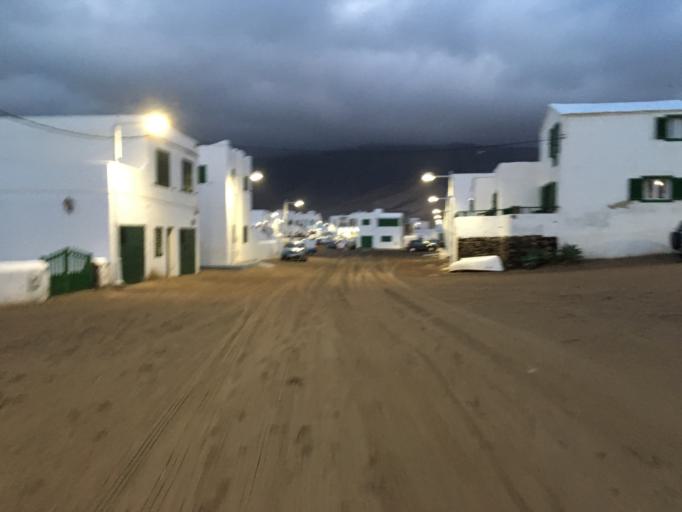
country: ES
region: Canary Islands
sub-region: Provincia de Las Palmas
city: Teguise
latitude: 29.1185
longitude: -13.5656
